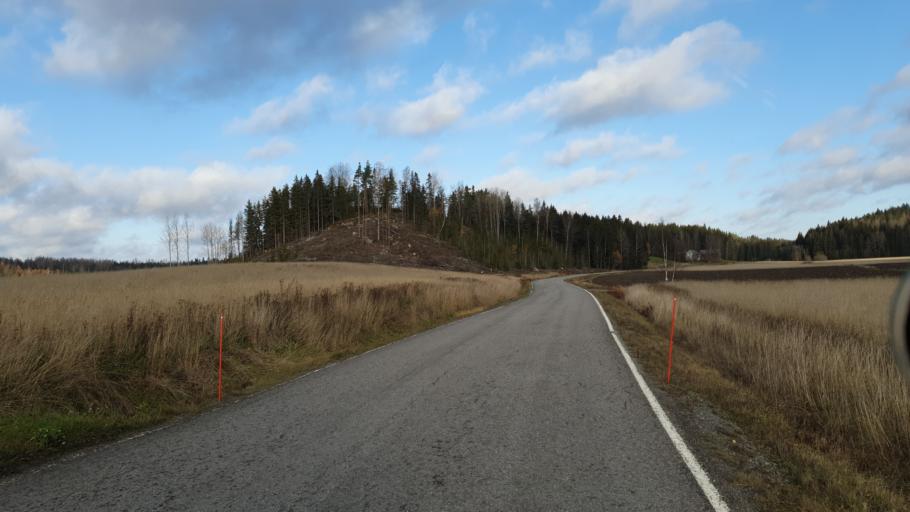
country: FI
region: Uusimaa
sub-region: Helsinki
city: Siuntio
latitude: 60.2550
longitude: 24.2989
